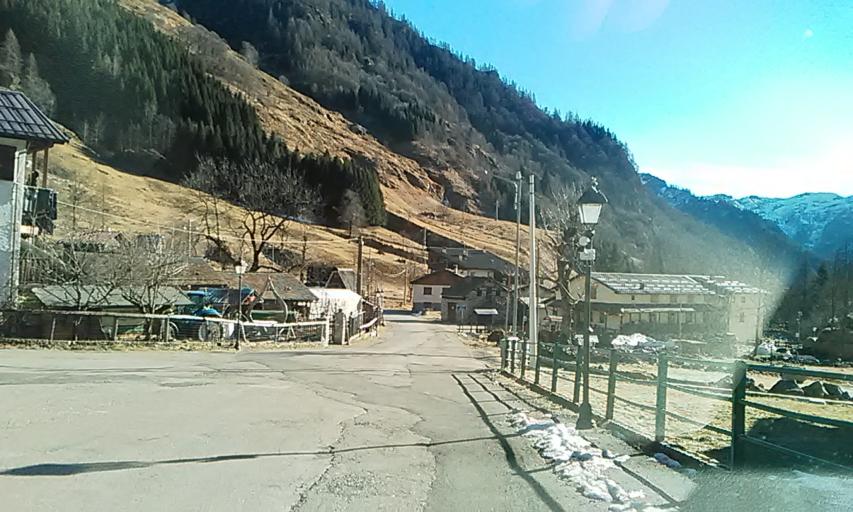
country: IT
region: Piedmont
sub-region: Provincia di Vercelli
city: Carcoforo
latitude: 45.9083
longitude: 8.0498
